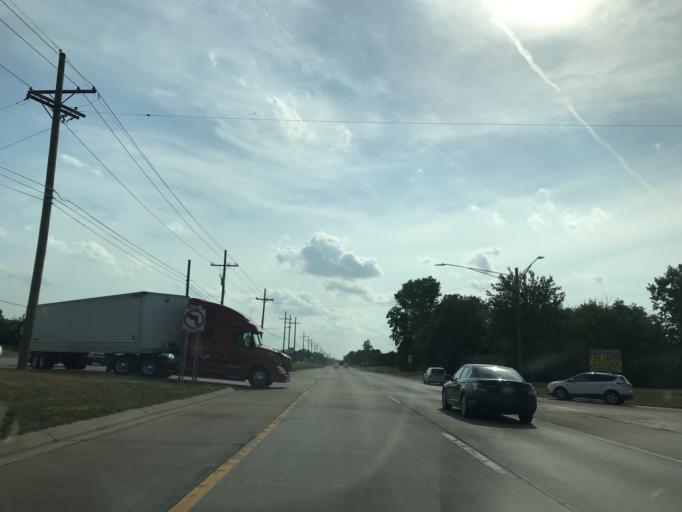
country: US
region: Michigan
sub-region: Wayne County
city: Canton
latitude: 42.2675
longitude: -83.5040
